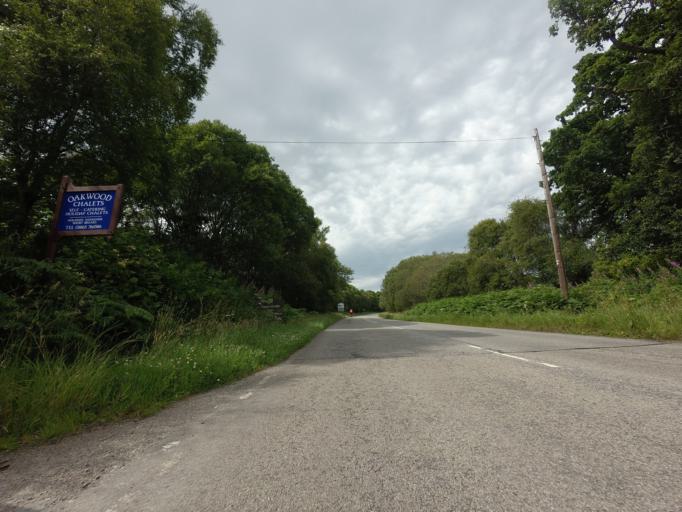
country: GB
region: Scotland
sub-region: Highland
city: Alness
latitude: 57.8752
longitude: -4.3562
